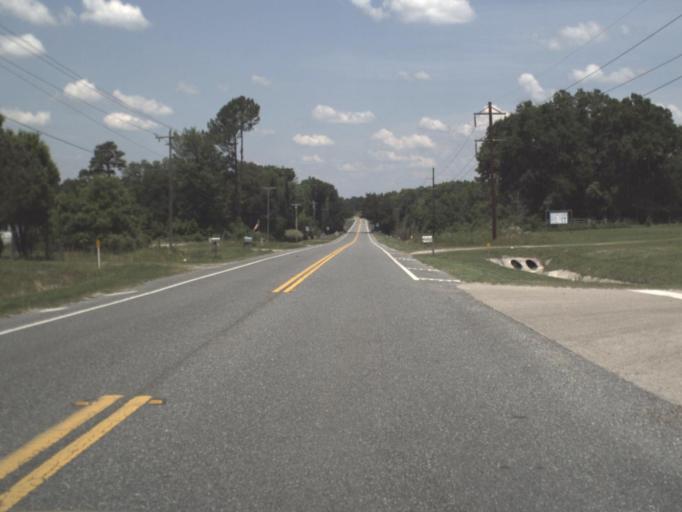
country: US
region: Florida
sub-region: Union County
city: Lake Butler
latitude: 29.9961
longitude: -82.2701
